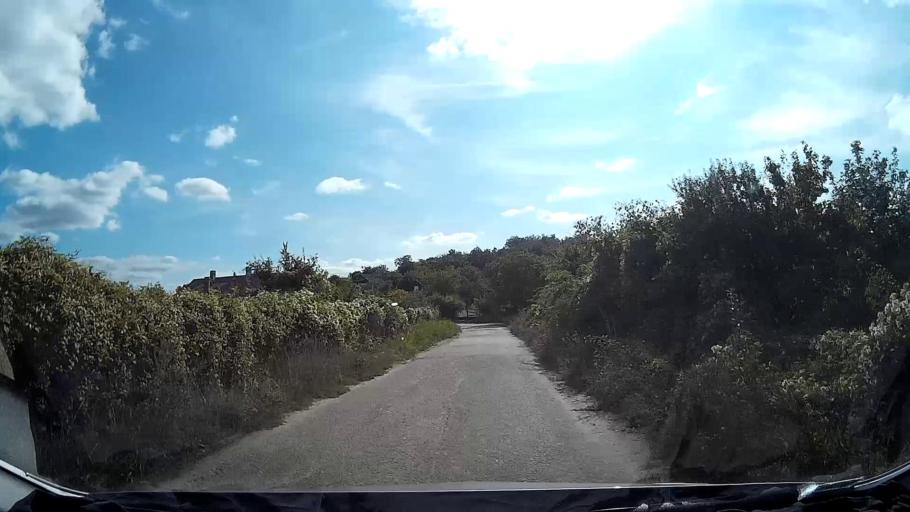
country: HU
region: Pest
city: Nagykovacsi
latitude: 47.6620
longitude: 19.0251
